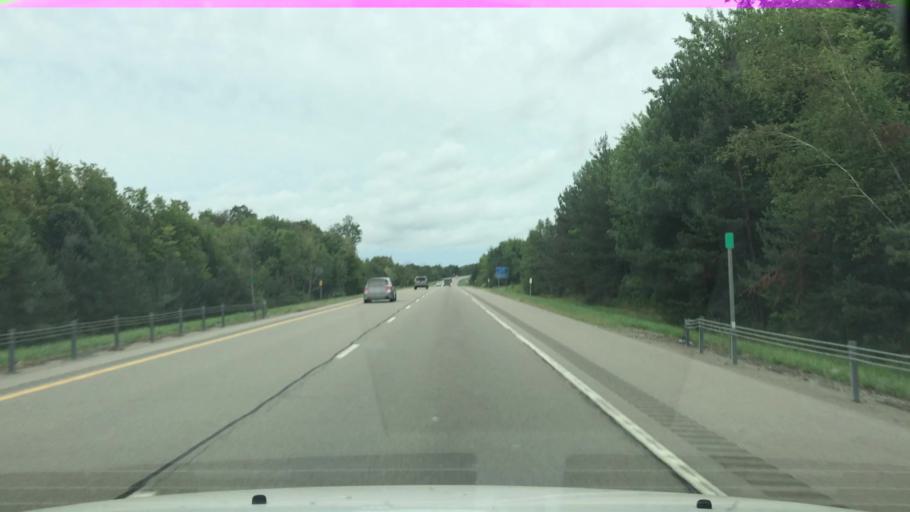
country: US
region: New York
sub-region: Erie County
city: North Boston
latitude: 42.6463
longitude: -78.7651
